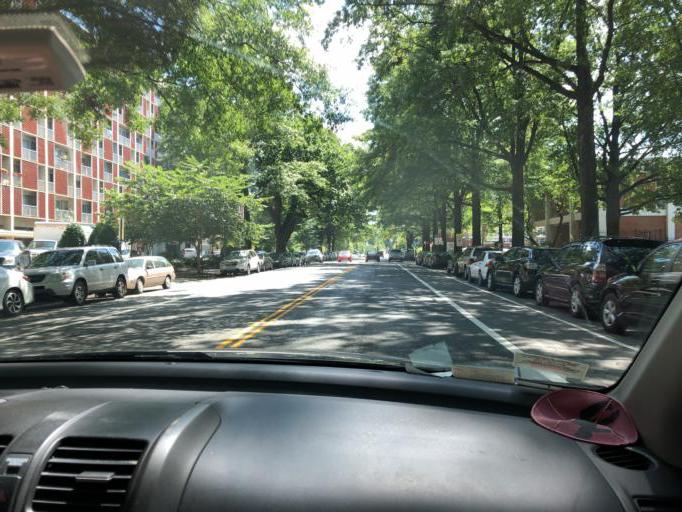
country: US
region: Washington, D.C.
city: Washington, D.C.
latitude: 38.8809
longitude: -77.0176
